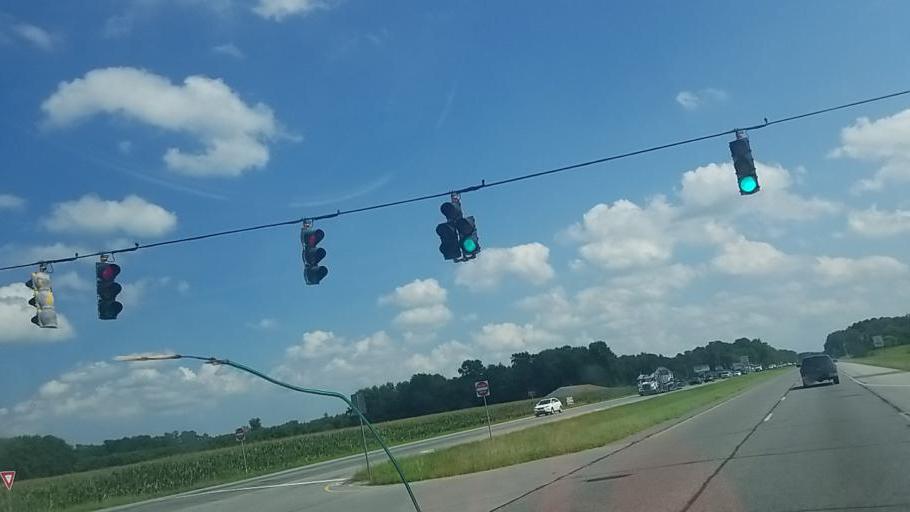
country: US
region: Delaware
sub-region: Sussex County
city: Georgetown
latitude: 38.7393
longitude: -75.4243
